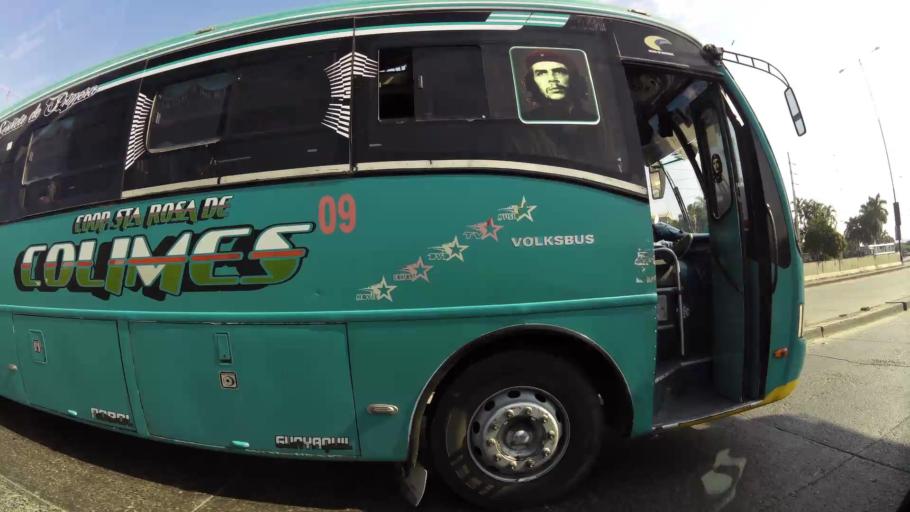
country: EC
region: Guayas
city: Eloy Alfaro
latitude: -2.0774
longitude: -79.9226
